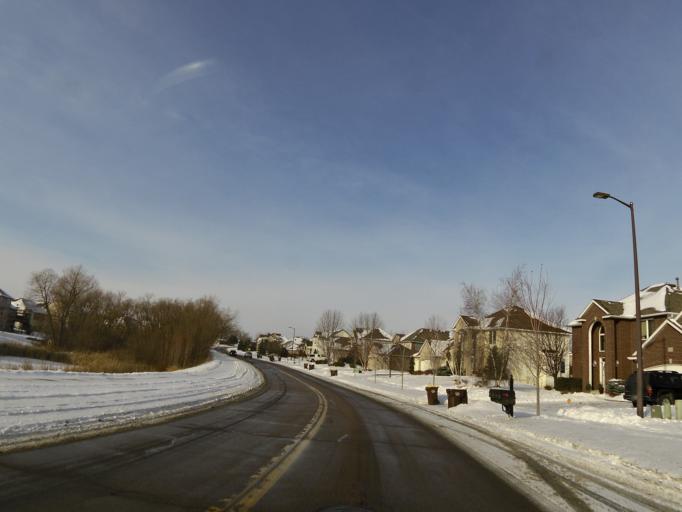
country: US
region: Minnesota
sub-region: Scott County
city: Prior Lake
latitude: 44.7281
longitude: -93.4516
